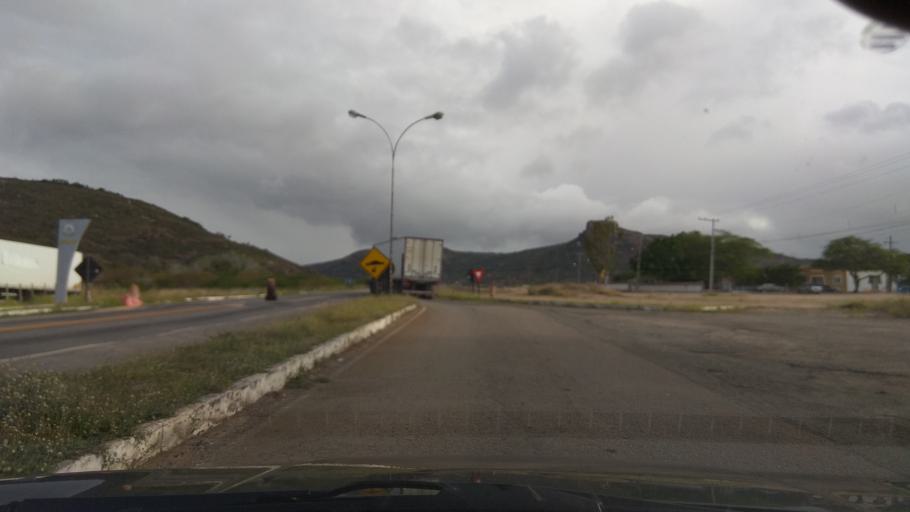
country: BR
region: Bahia
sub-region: Amargosa
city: Amargosa
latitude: -12.8562
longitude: -39.8480
